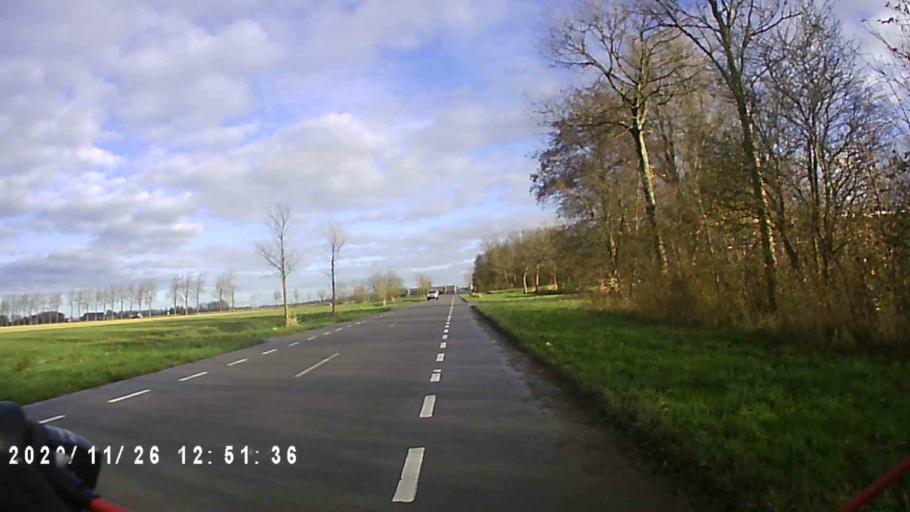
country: NL
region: Groningen
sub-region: Gemeente Appingedam
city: Appingedam
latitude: 53.3527
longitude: 6.7838
